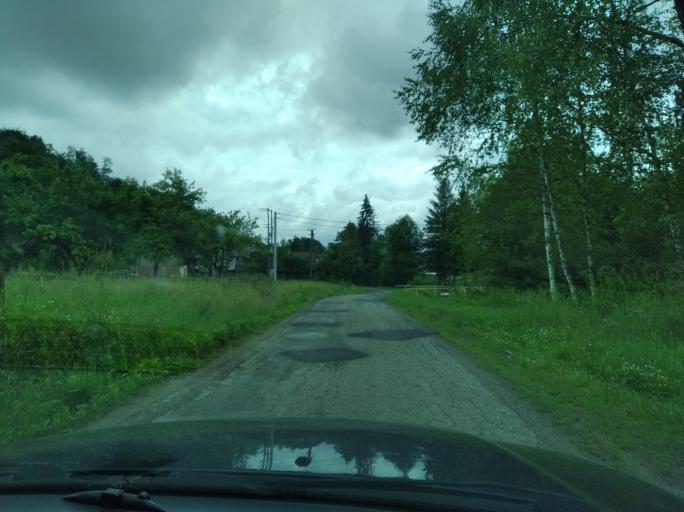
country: PL
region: Subcarpathian Voivodeship
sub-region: Powiat przemyski
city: Nienadowa
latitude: 49.8549
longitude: 22.4129
